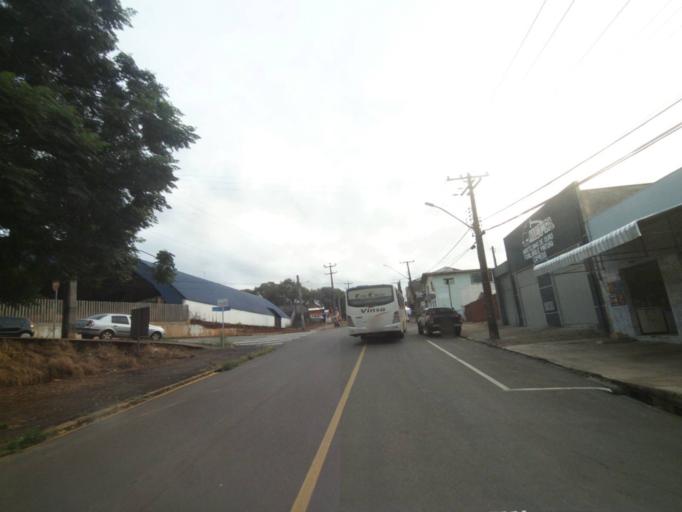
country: BR
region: Parana
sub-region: Telemaco Borba
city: Telemaco Borba
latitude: -24.3315
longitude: -50.6339
